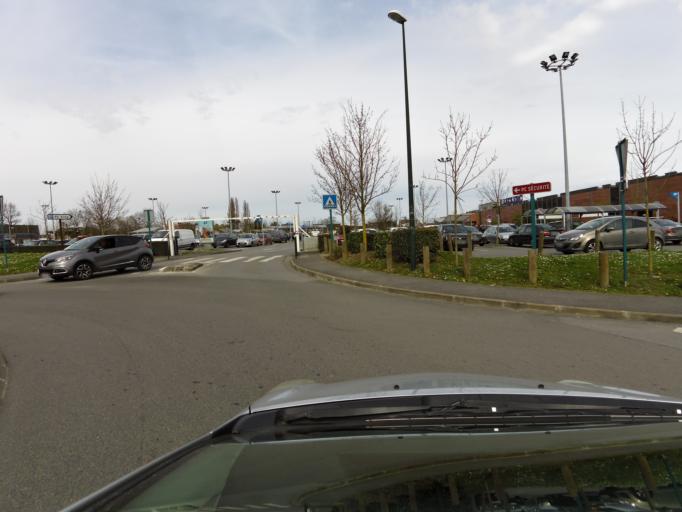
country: FR
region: Ile-de-France
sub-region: Departement de Seine-et-Marne
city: Villeparisis
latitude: 48.9523
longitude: 2.6080
